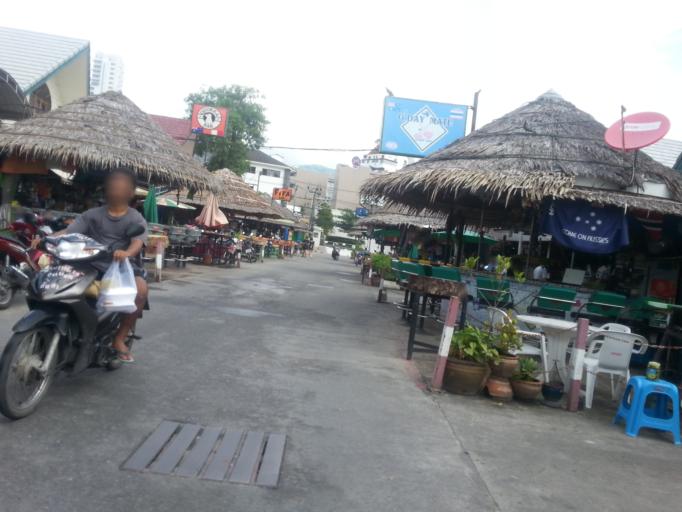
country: TH
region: Phuket
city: Patong
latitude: 7.8873
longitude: 98.2956
